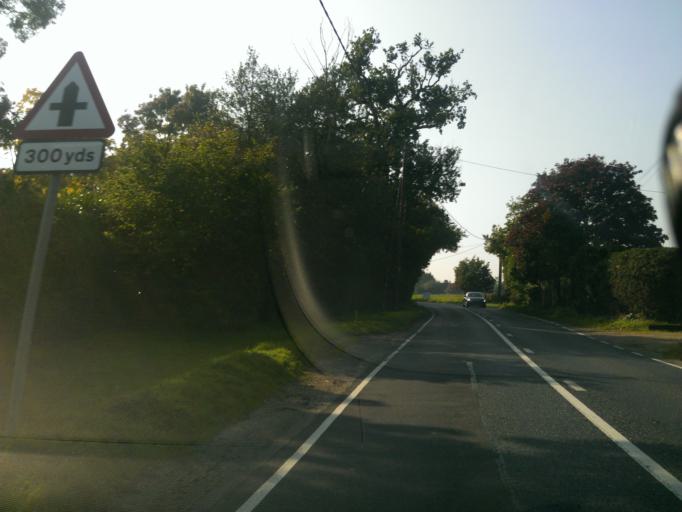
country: GB
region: England
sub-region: Essex
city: Layer de la Haye
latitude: 51.8552
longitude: 0.8184
